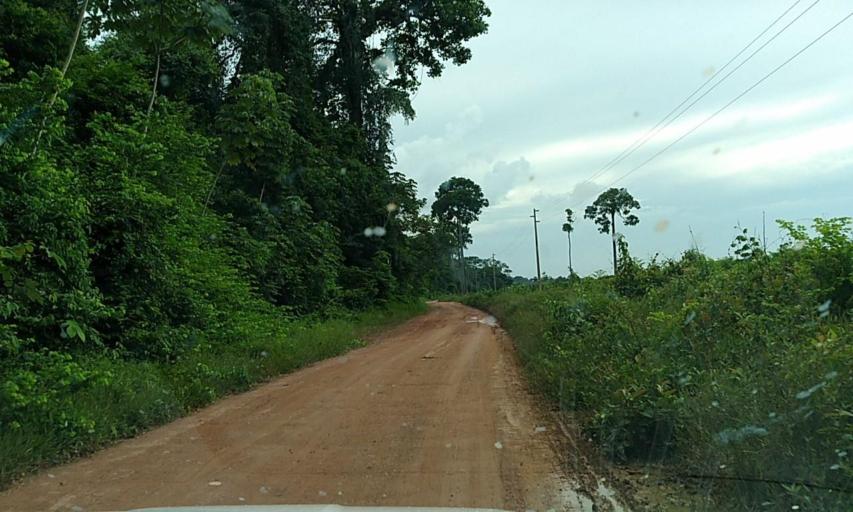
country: BR
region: Para
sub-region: Senador Jose Porfirio
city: Senador Jose Porfirio
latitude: -2.5443
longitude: -51.8603
